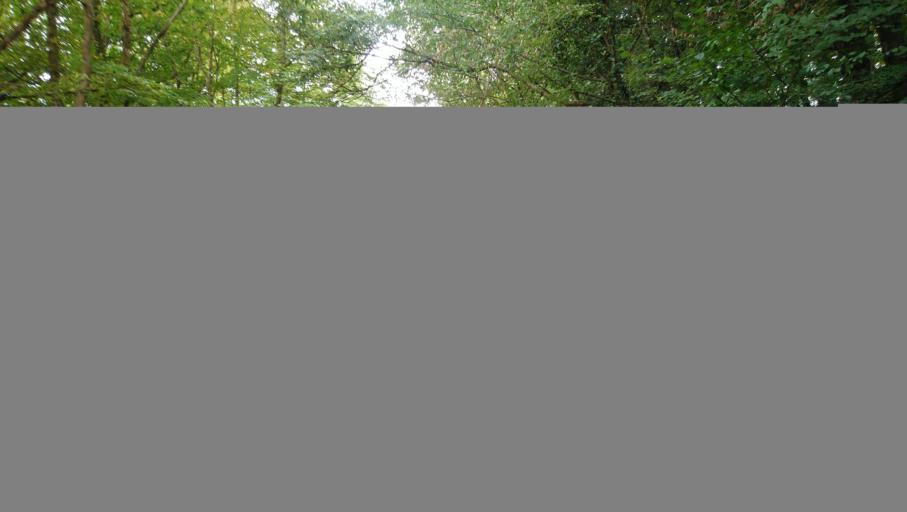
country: LU
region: Luxembourg
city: Belvaux
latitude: 49.5039
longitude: 5.9150
